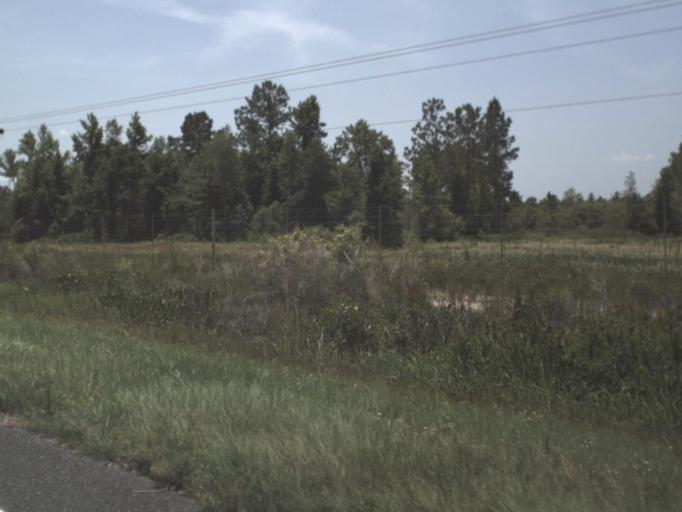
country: US
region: Florida
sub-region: Taylor County
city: Steinhatchee
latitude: 29.8251
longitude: -83.3565
